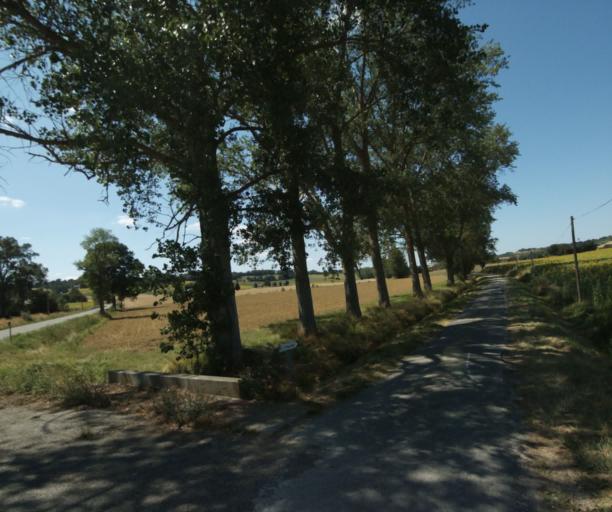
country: FR
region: Midi-Pyrenees
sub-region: Departement de la Haute-Garonne
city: Saint-Felix-Lauragais
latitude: 43.4853
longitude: 1.8800
